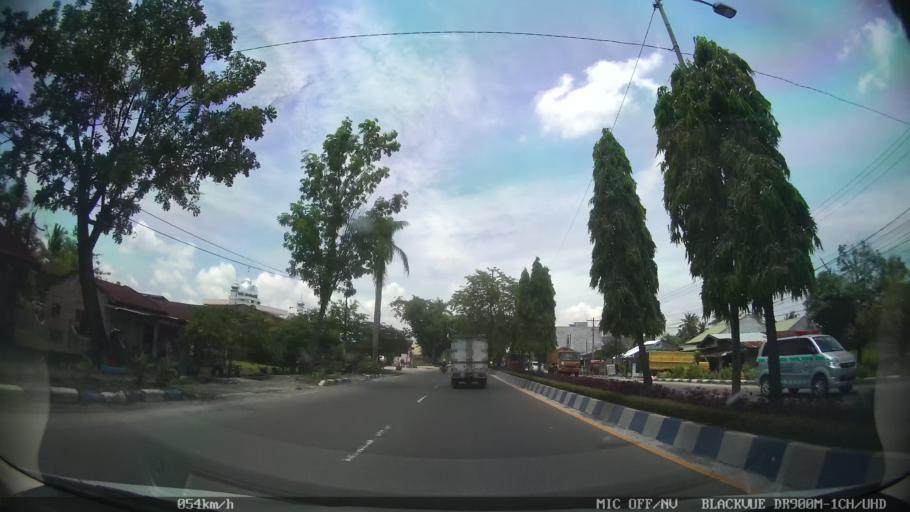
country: ID
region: North Sumatra
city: Percut
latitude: 3.5519
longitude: 98.8592
